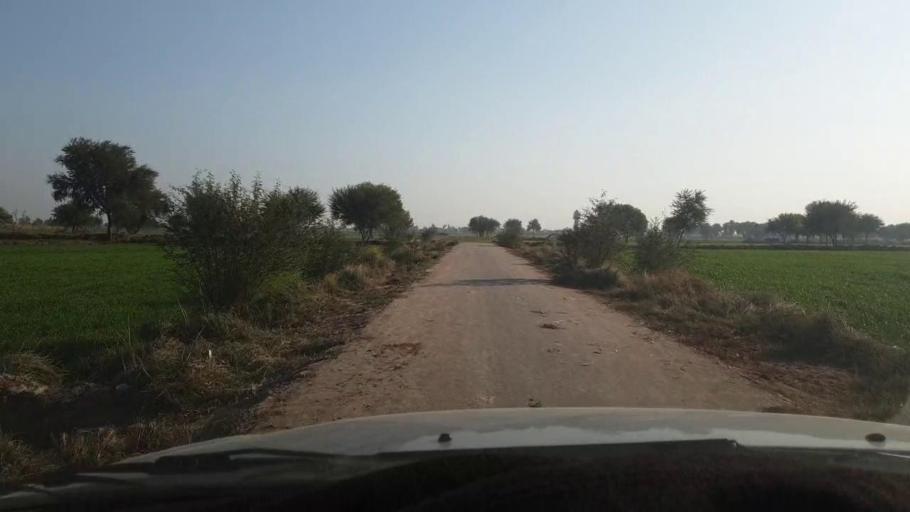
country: PK
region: Sindh
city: Mirpur Mathelo
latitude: 28.0177
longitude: 69.6044
